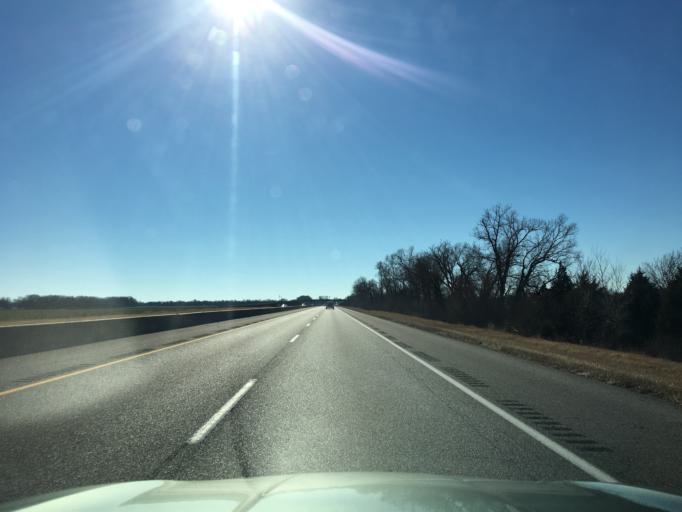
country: US
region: Kansas
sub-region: Sumner County
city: Belle Plaine
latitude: 37.4272
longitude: -97.3214
